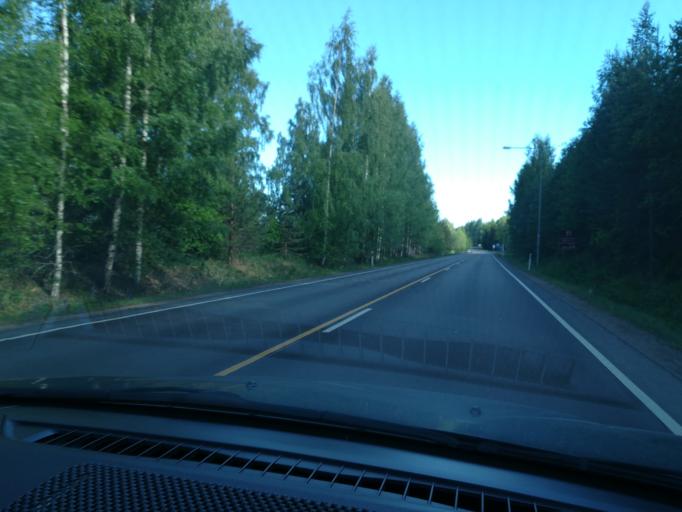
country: FI
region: Southern Savonia
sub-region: Mikkeli
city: Puumala
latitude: 61.5143
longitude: 28.1753
